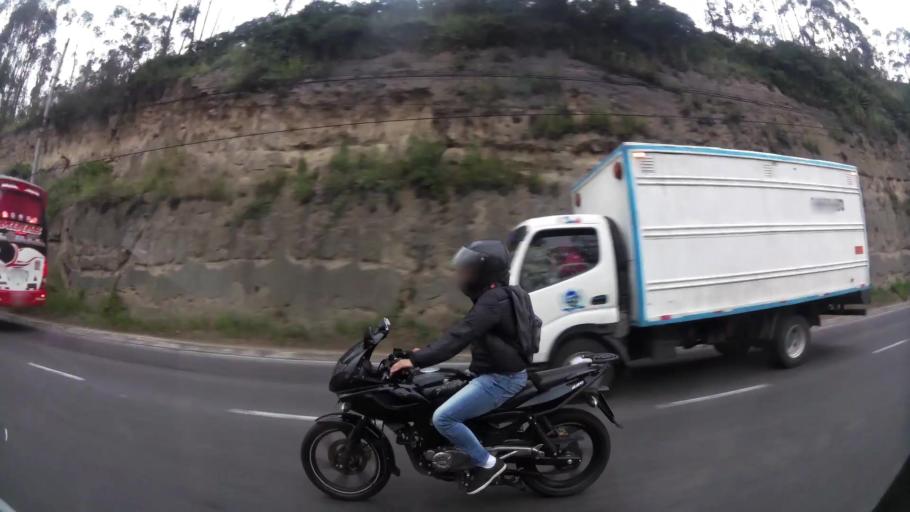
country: EC
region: Pichincha
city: Quito
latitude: -0.1020
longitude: -78.4635
